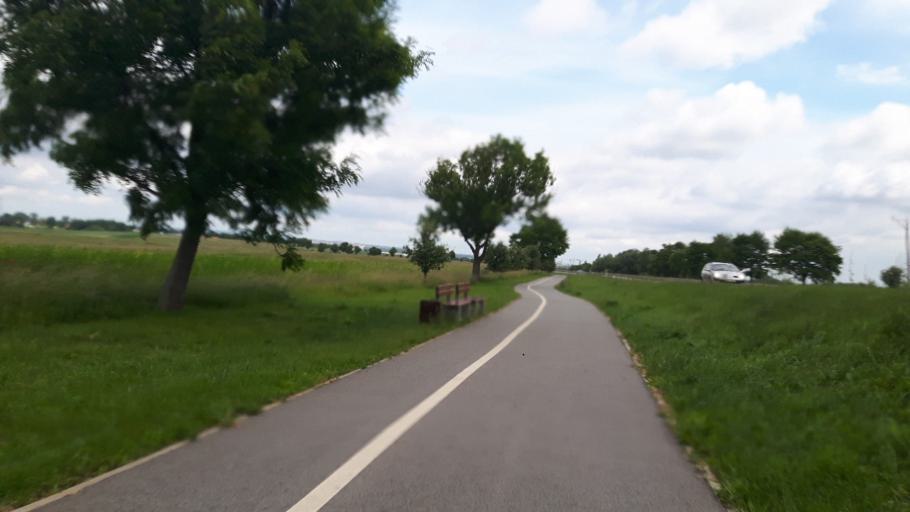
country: PL
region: West Pomeranian Voivodeship
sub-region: Powiat policki
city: Przeclaw
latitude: 53.3615
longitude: 14.4691
